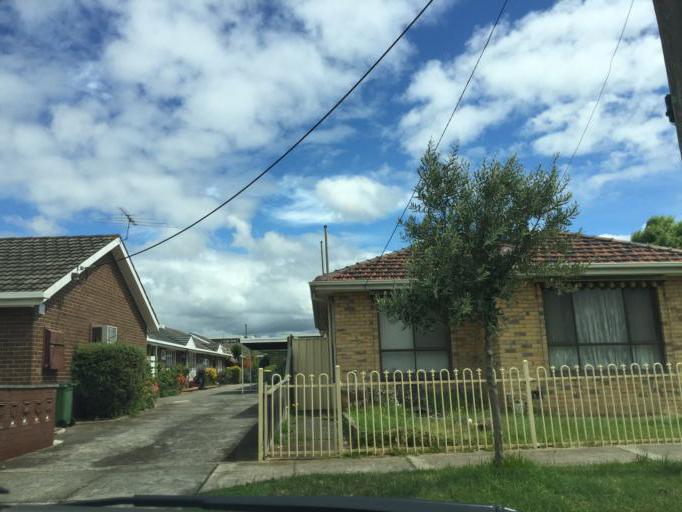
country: AU
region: Victoria
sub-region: Maribyrnong
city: West Footscray
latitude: -37.7971
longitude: 144.8696
